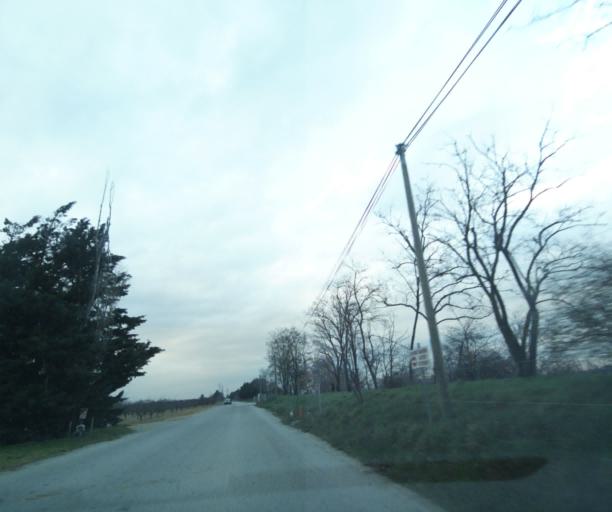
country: FR
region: Rhone-Alpes
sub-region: Departement de la Drome
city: Bourg-les-Valence
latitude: 44.9772
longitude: 4.8888
